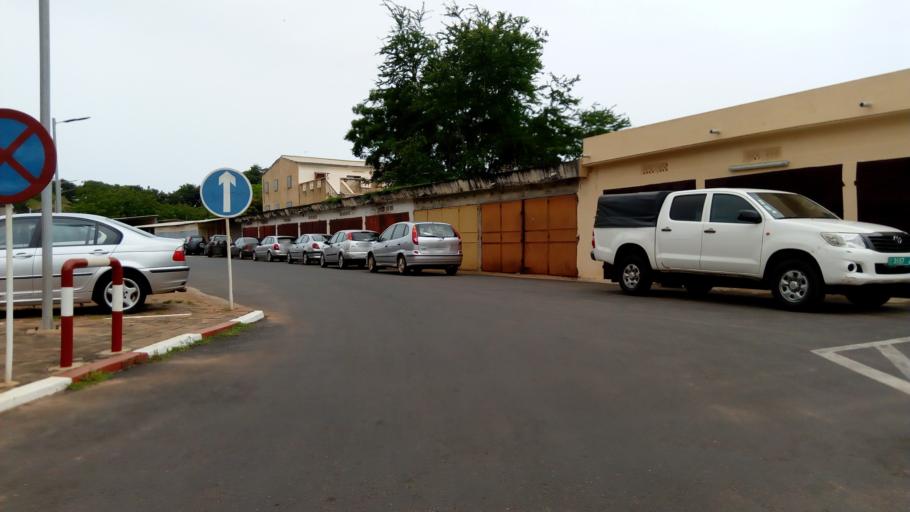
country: TG
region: Maritime
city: Lome
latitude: 6.1280
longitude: 1.2163
